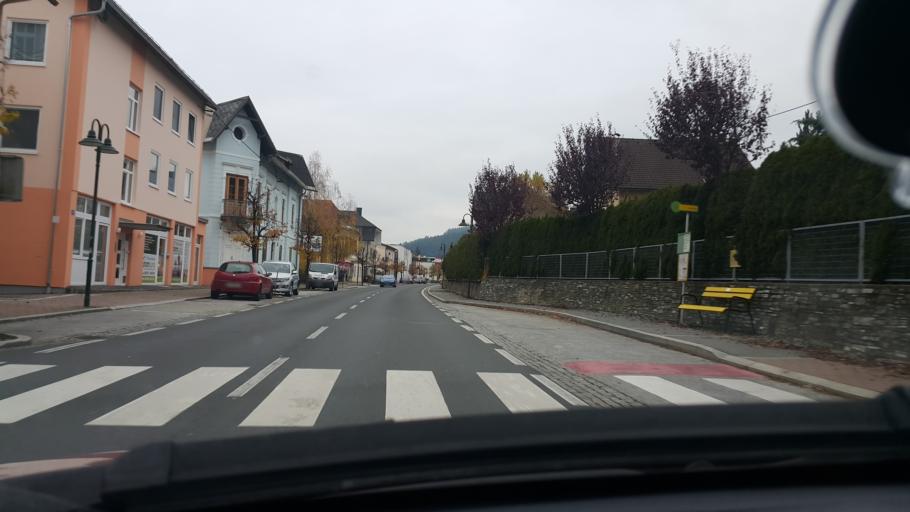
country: AT
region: Carinthia
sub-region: Politischer Bezirk Klagenfurt Land
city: Keutschach am See
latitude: 46.6262
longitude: 14.2171
